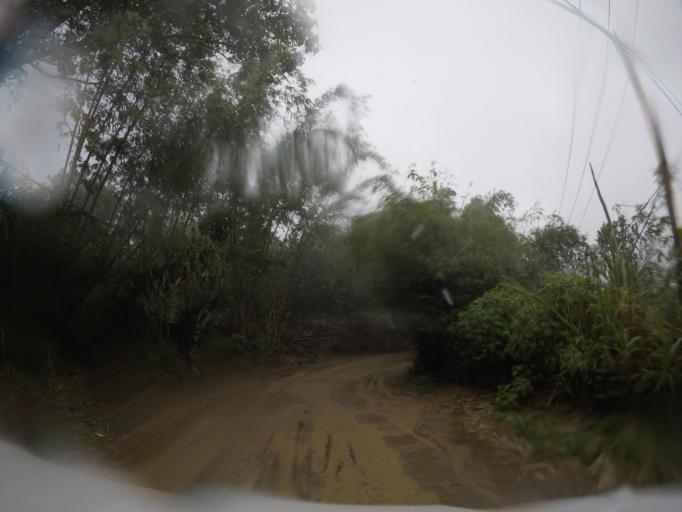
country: TL
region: Baucau
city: Venilale
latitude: -8.6412
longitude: 126.4058
